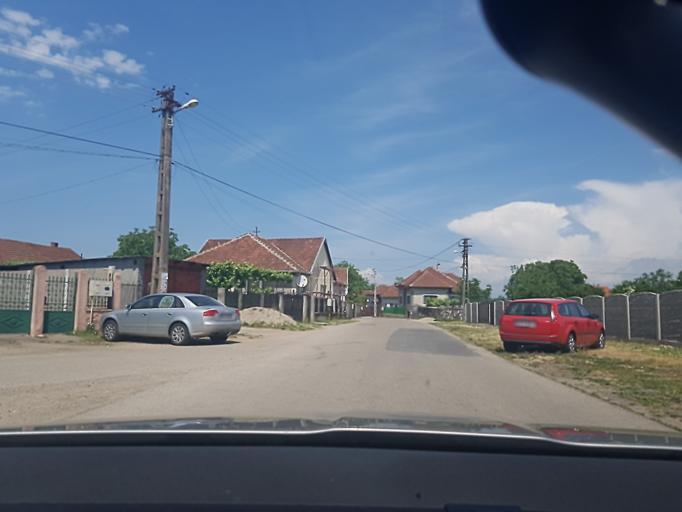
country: RO
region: Hunedoara
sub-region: Comuna Calan
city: Calan
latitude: 45.7392
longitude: 23.0087
